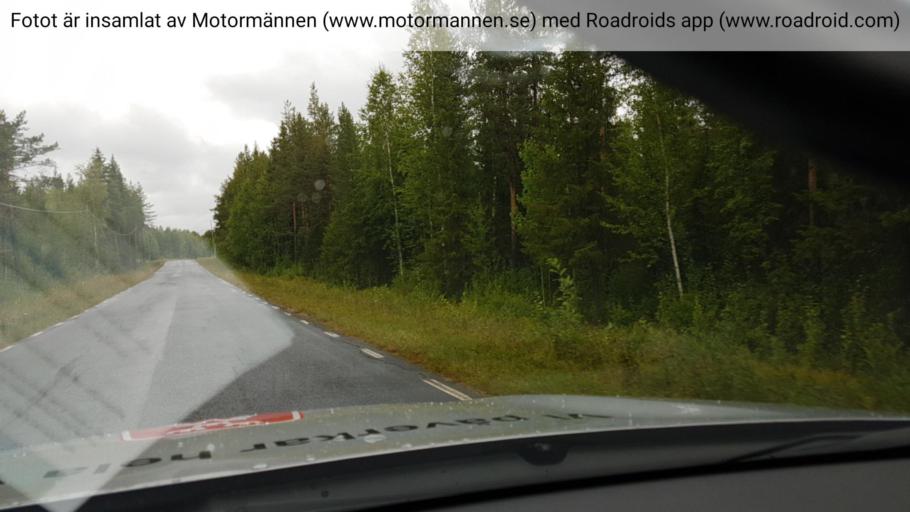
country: SE
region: Norrbotten
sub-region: Alvsbyns Kommun
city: AElvsbyn
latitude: 66.0797
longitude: 20.9104
